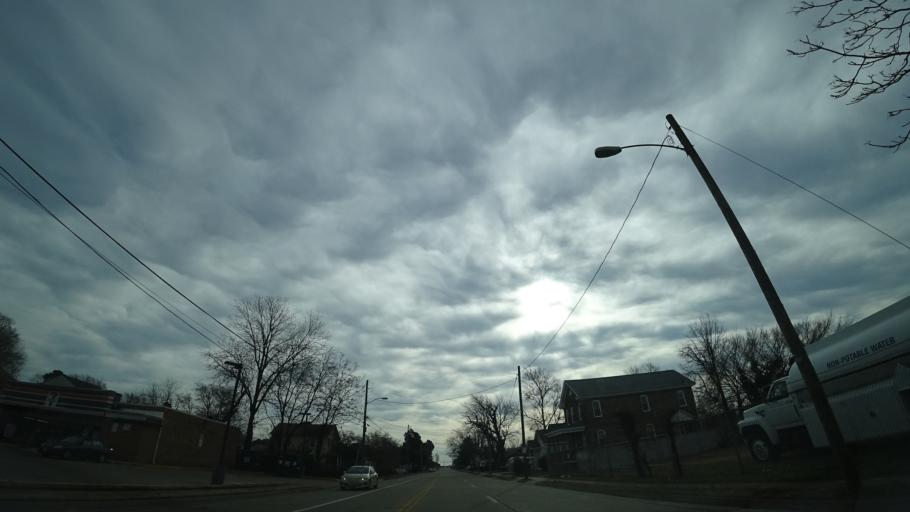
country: US
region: Virginia
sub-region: City of Hampton
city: East Hampton
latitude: 37.0213
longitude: -76.3183
